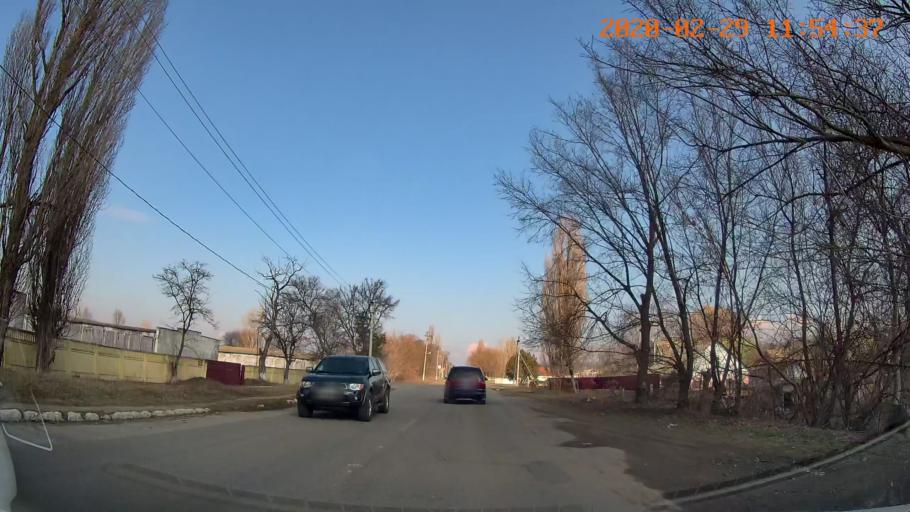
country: MD
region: Telenesti
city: Ribnita
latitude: 47.7853
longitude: 28.9956
